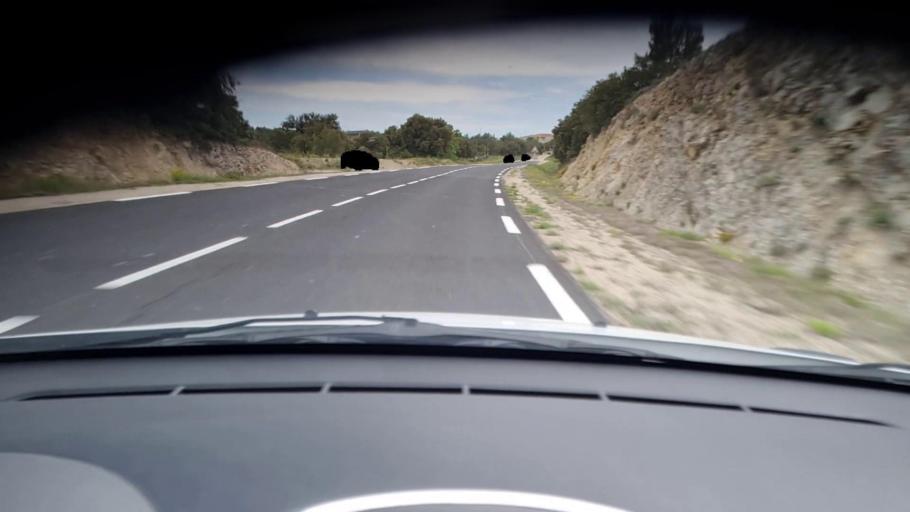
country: FR
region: Languedoc-Roussillon
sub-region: Departement du Gard
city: Poulx
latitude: 43.8893
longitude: 4.3854
